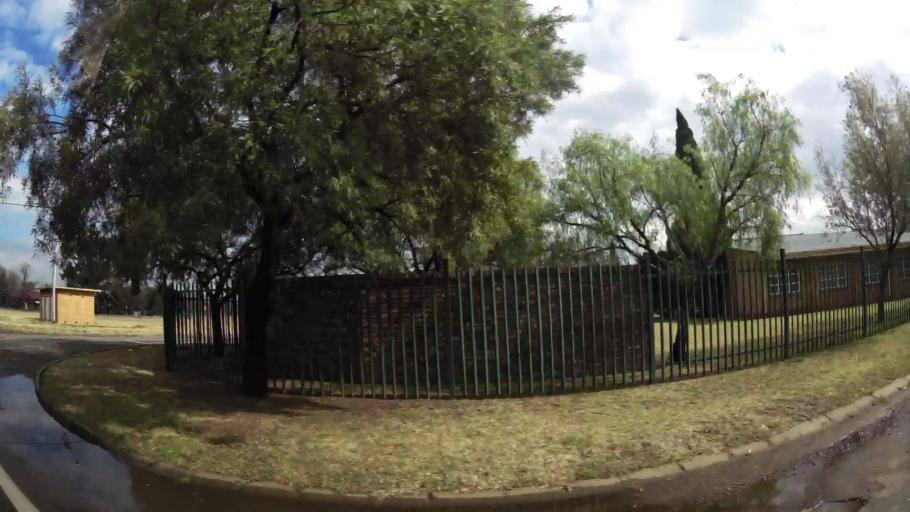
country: ZA
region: Gauteng
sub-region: Sedibeng District Municipality
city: Vereeniging
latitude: -26.6514
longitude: 27.9742
